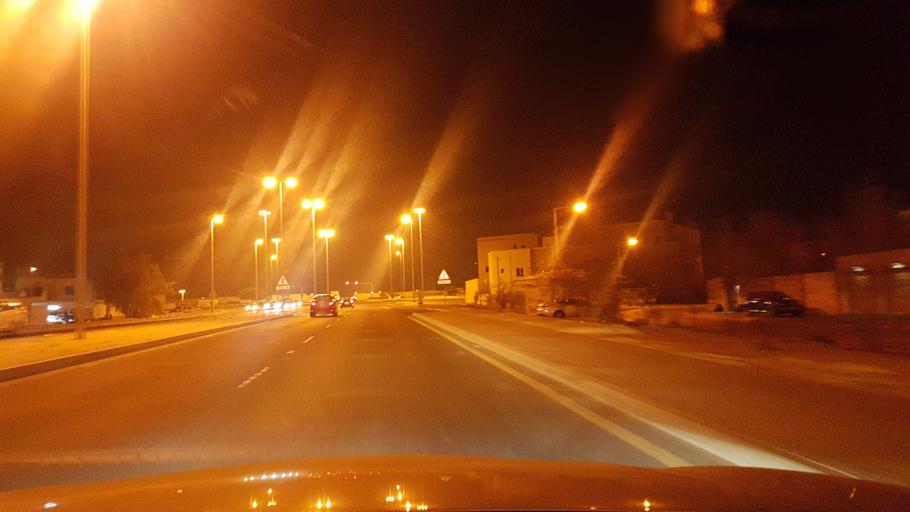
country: BH
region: Central Governorate
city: Madinat Hamad
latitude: 26.0972
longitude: 50.5083
